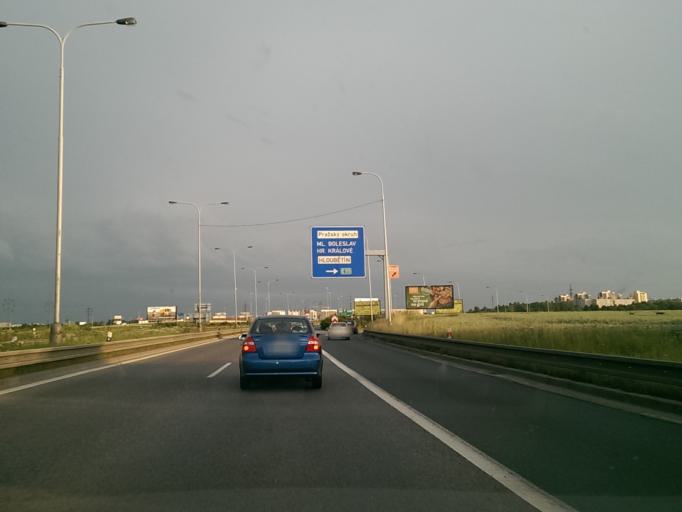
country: CZ
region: Praha
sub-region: Praha 9
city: Strizkov
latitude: 50.1427
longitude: 14.4944
